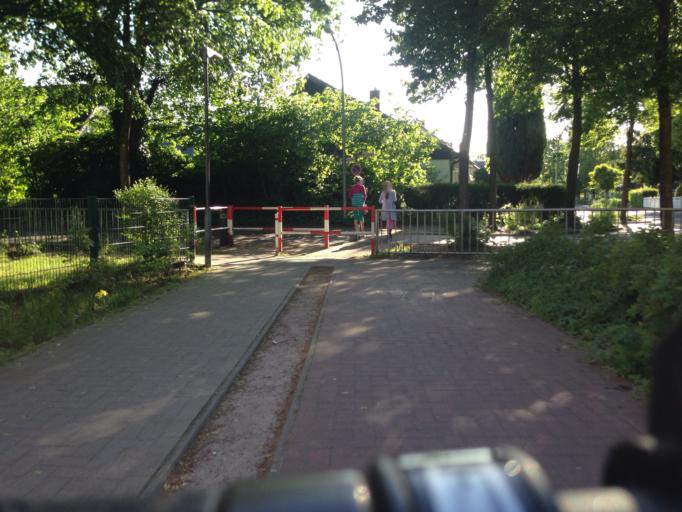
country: DE
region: Schleswig-Holstein
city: Barsbuettel
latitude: 53.5720
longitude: 10.1629
